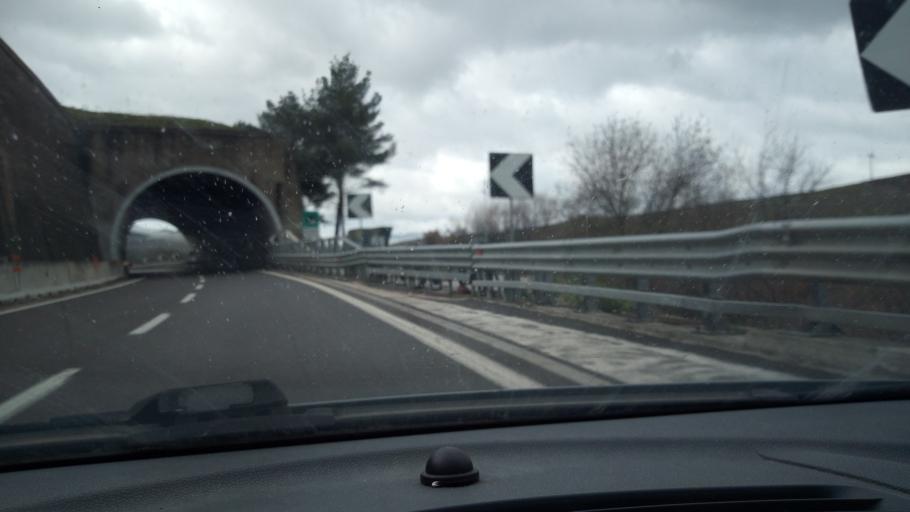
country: IT
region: Apulia
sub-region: Provincia di Foggia
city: Sant'Agata di Puglia
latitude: 41.0977
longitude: 15.3878
